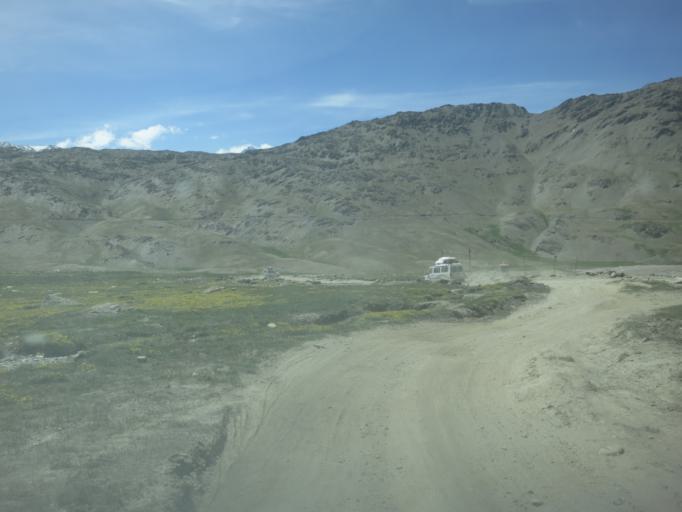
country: IN
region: Himachal Pradesh
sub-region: Kulu
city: Manali
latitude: 32.4053
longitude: 77.6440
